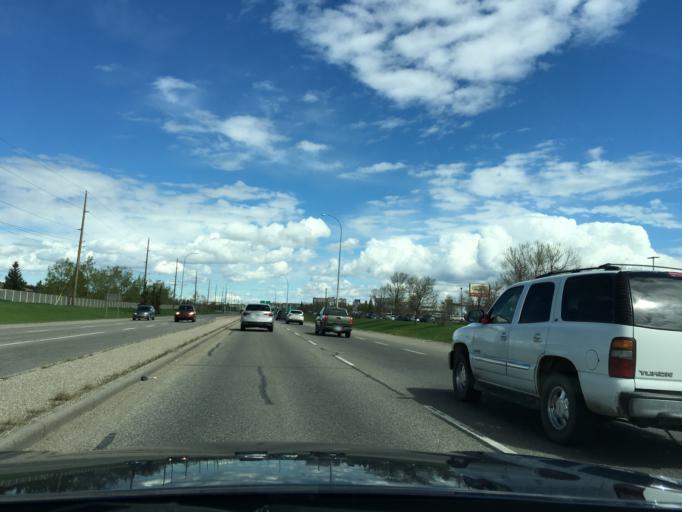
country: CA
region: Alberta
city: Calgary
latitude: 51.0596
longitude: -114.0017
